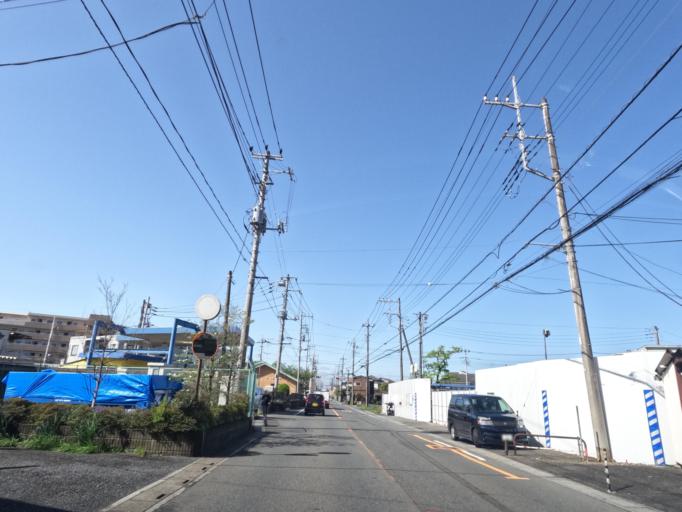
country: JP
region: Saitama
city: Yono
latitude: 35.8722
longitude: 139.6137
